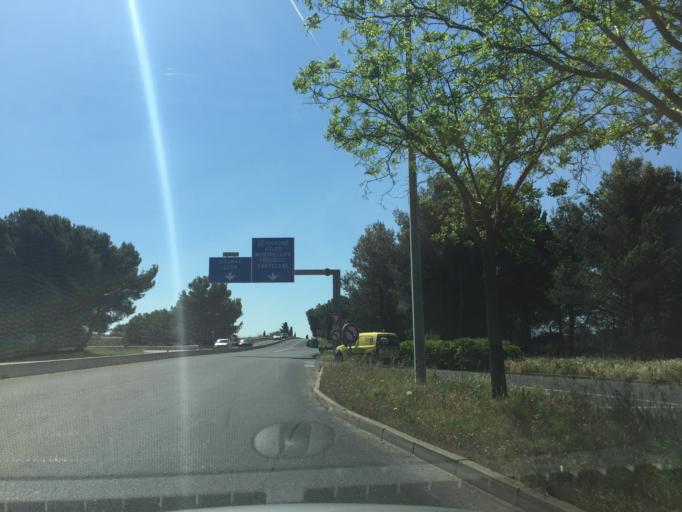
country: FR
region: Languedoc-Roussillon
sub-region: Departement du Gard
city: Remoulins
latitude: 43.9364
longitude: 4.5991
